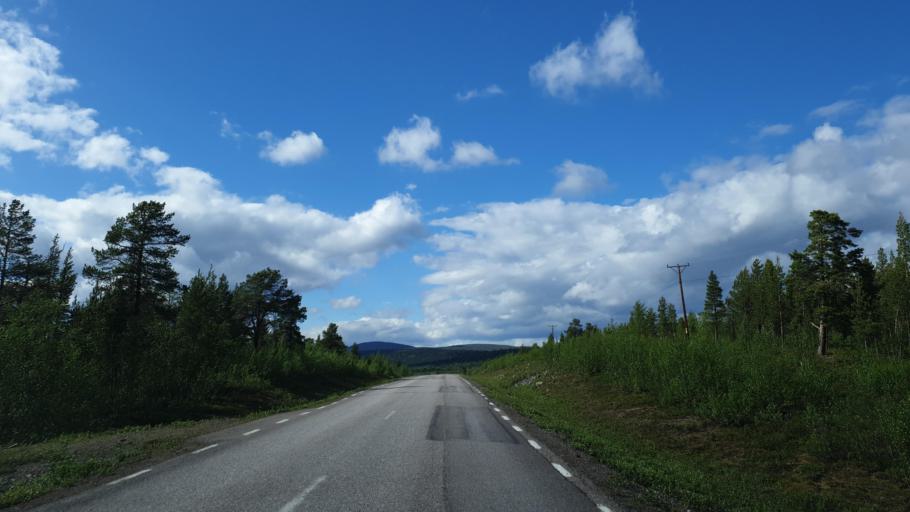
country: SE
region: Norrbotten
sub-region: Kiruna Kommun
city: Kiruna
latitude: 67.7750
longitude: 19.9700
